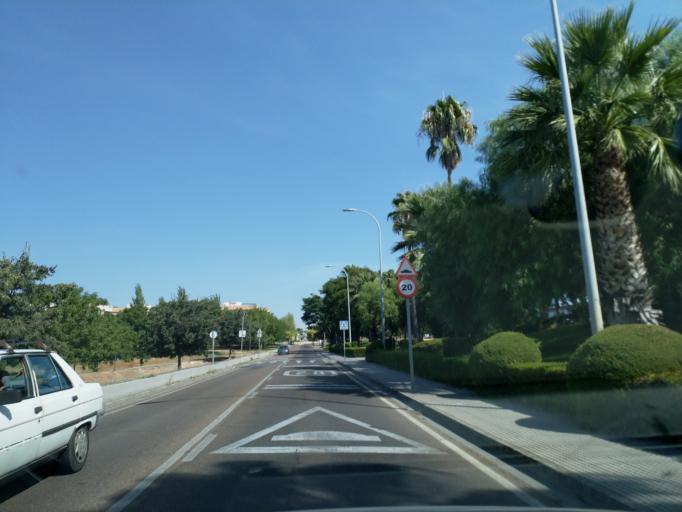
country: ES
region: Extremadura
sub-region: Provincia de Badajoz
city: Merida
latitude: 38.9308
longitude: -6.3470
